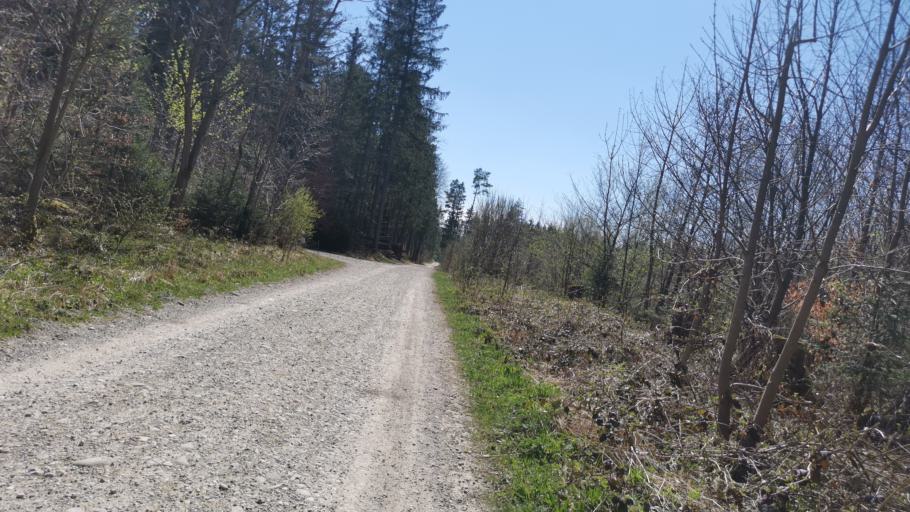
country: DE
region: Bavaria
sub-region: Upper Bavaria
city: Planegg
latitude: 48.0800
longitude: 11.4223
